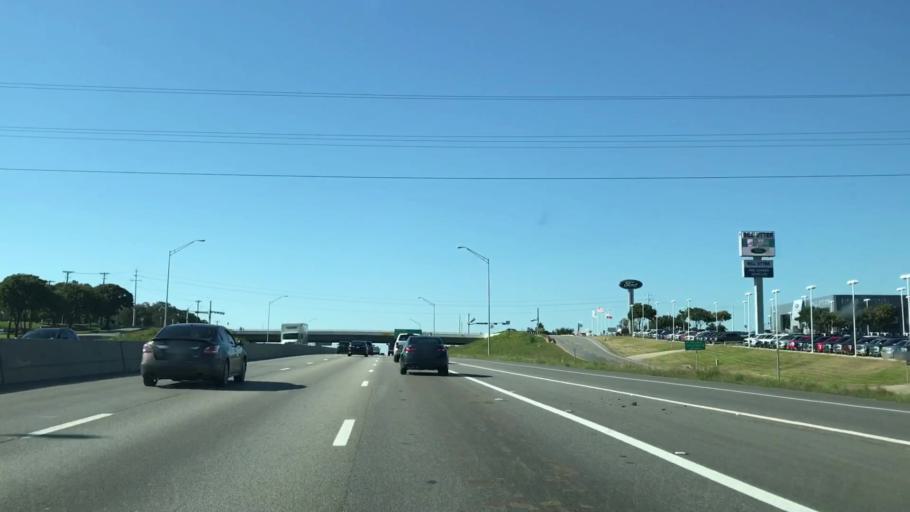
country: US
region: Texas
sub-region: Denton County
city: Corinth
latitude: 33.1605
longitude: -97.0709
